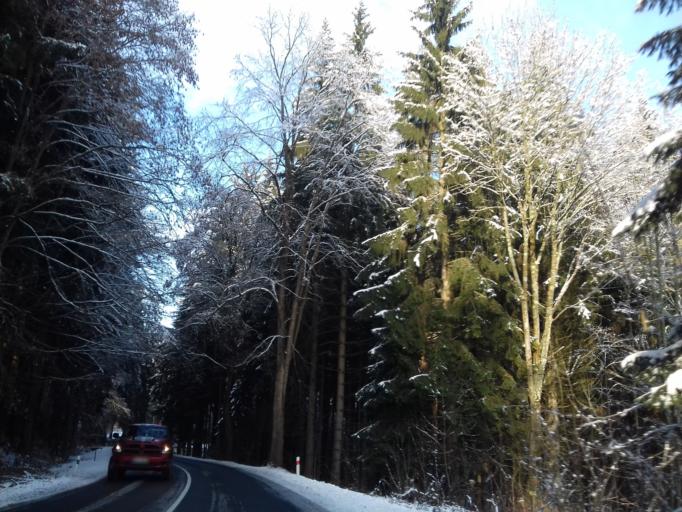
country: CZ
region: Plzensky
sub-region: Okres Domazlice
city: Klenci pod Cerchovem
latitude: 49.4159
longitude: 12.8058
